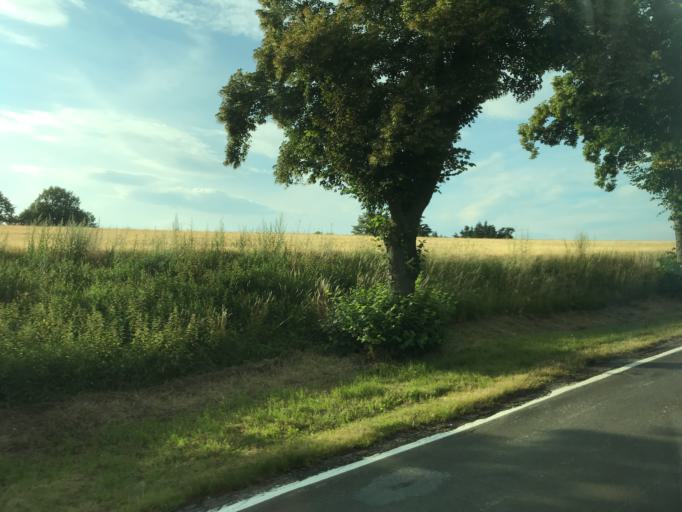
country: CZ
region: Jihocesky
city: Rudolfov
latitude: 49.0005
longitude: 14.5515
